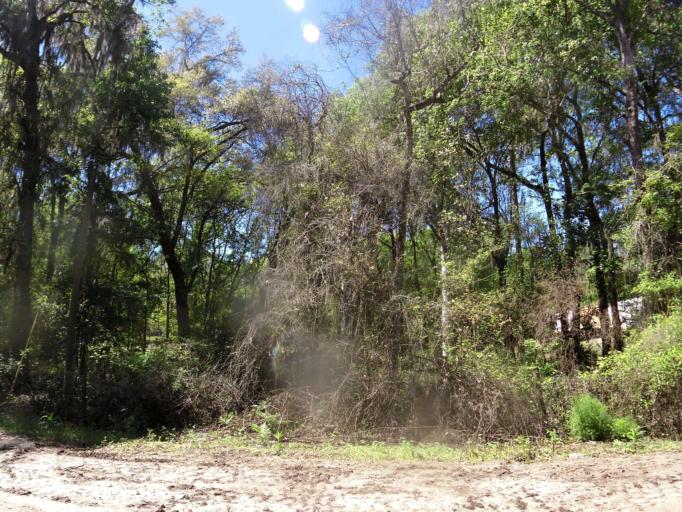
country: US
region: Florida
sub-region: Bradford County
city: Starke
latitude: 30.0538
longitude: -82.0554
